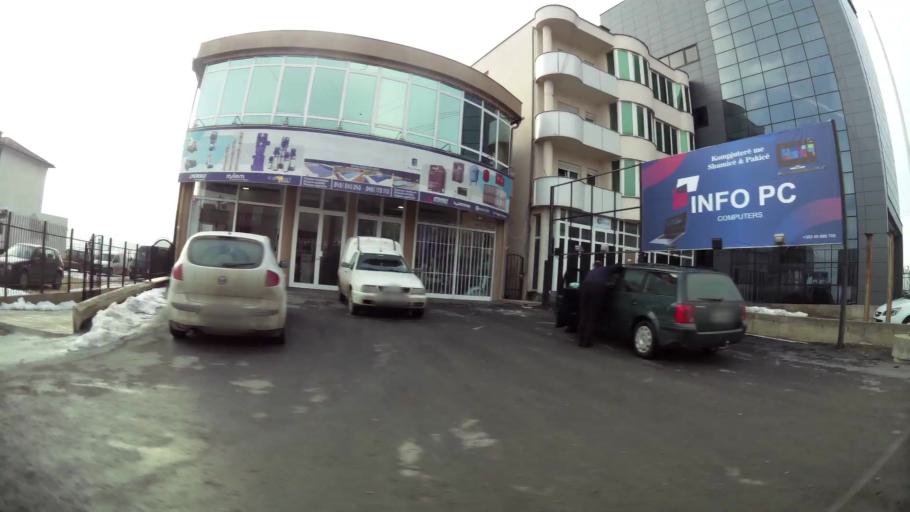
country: XK
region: Pristina
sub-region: Komuna e Prishtines
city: Pristina
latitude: 42.6265
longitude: 21.1612
